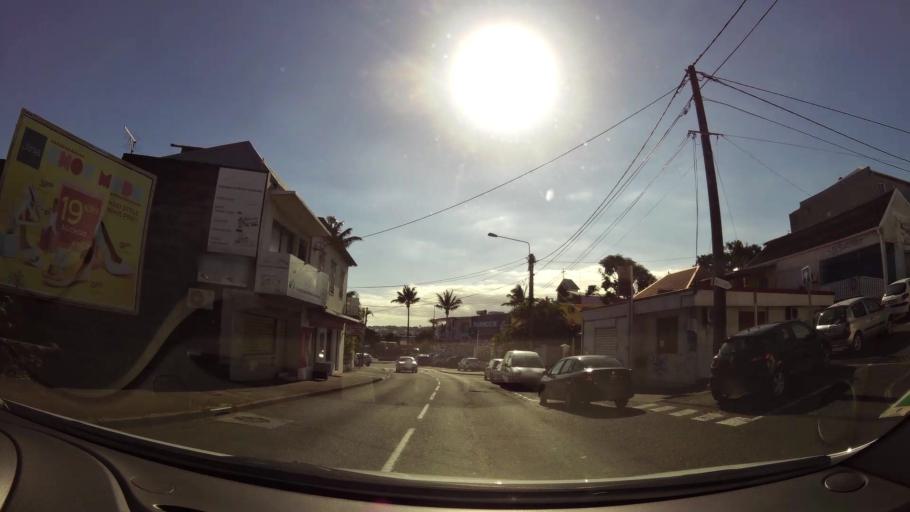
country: RE
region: Reunion
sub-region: Reunion
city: Saint-Pierre
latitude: -21.3433
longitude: 55.4821
